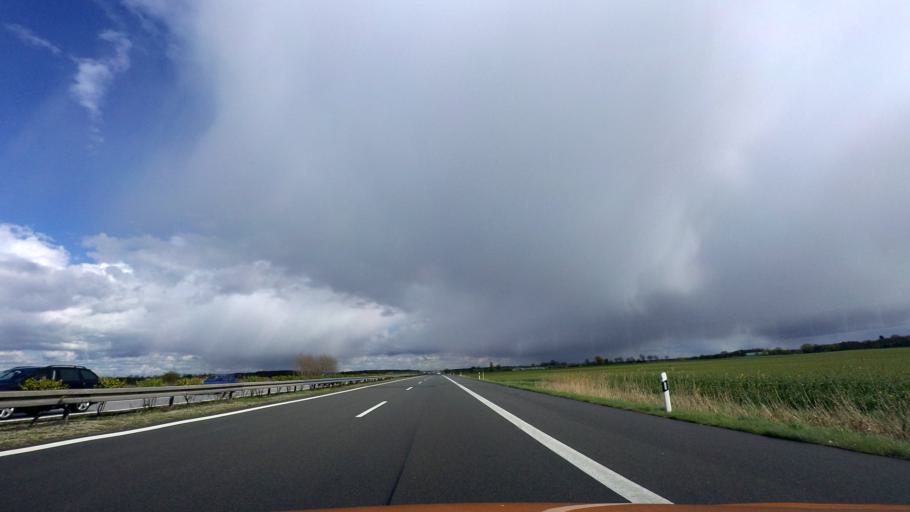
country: DE
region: Mecklenburg-Vorpommern
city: Hagenow
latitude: 53.4914
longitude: 11.1597
